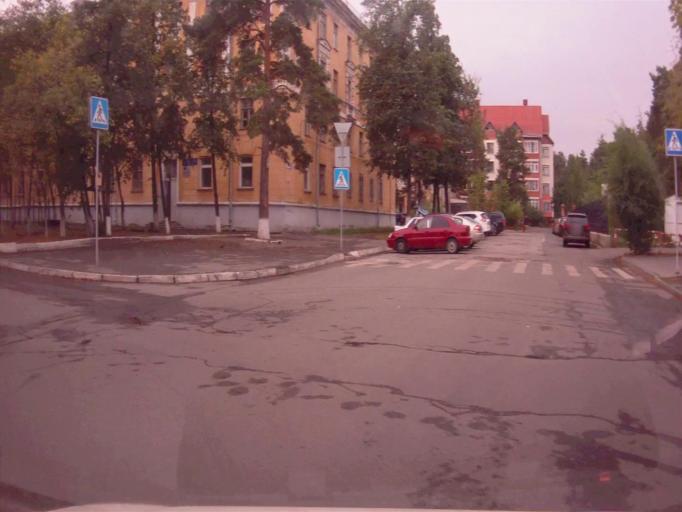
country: RU
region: Chelyabinsk
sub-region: Gorod Chelyabinsk
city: Chelyabinsk
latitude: 55.1606
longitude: 61.3678
